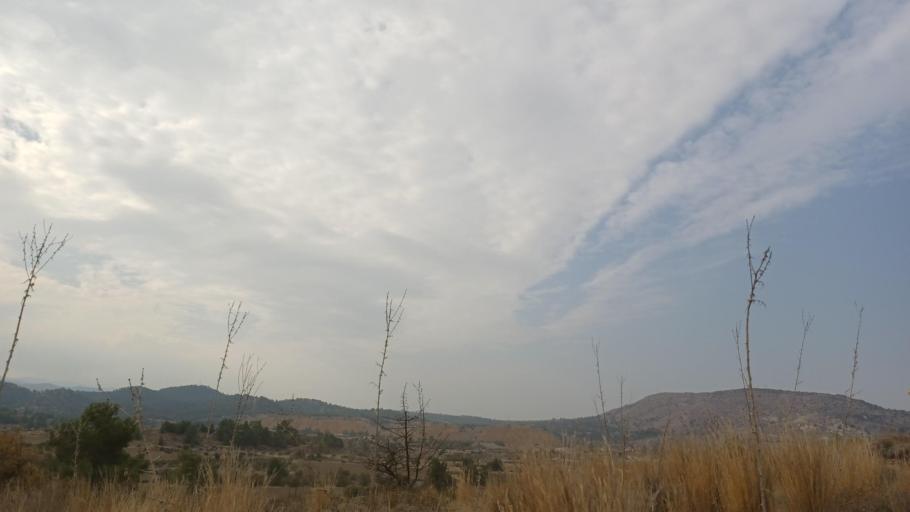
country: CY
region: Lefkosia
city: Klirou
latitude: 35.0342
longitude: 33.1382
